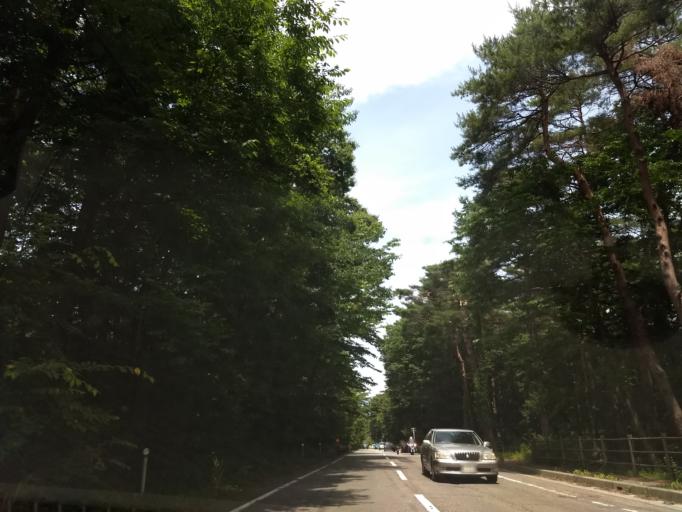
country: JP
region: Yamanashi
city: Fujikawaguchiko
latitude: 35.4484
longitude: 138.8187
